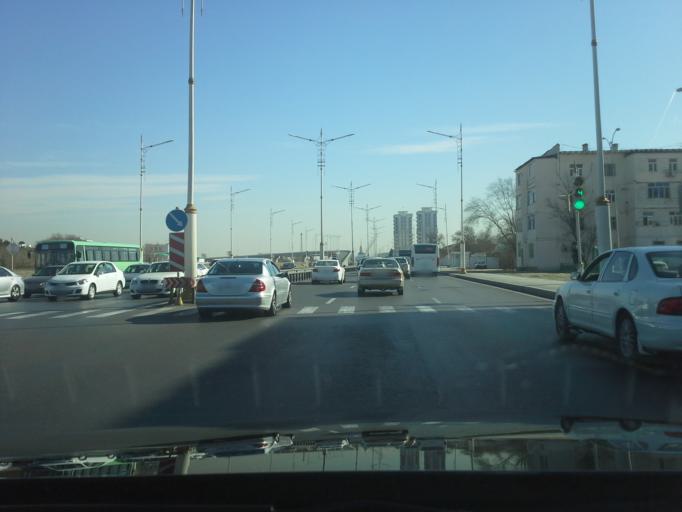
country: TM
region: Ahal
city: Ashgabat
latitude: 37.9508
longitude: 58.3811
